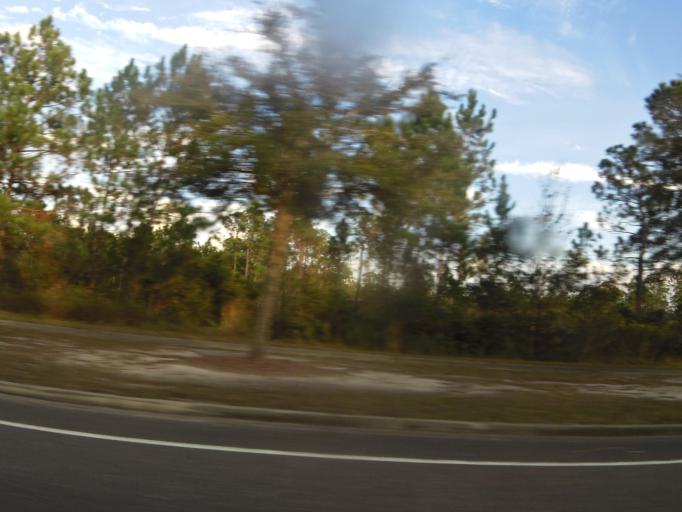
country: US
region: Florida
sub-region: Duval County
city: Baldwin
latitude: 30.2580
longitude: -81.8864
